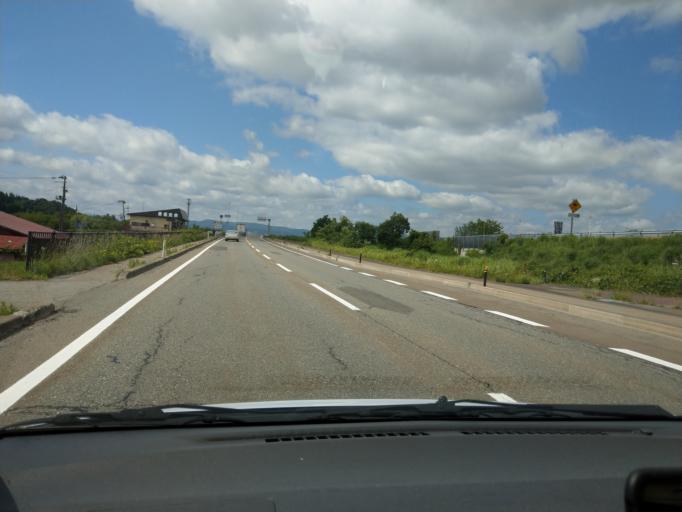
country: JP
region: Akita
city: Yuzawa
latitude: 39.2123
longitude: 140.5128
